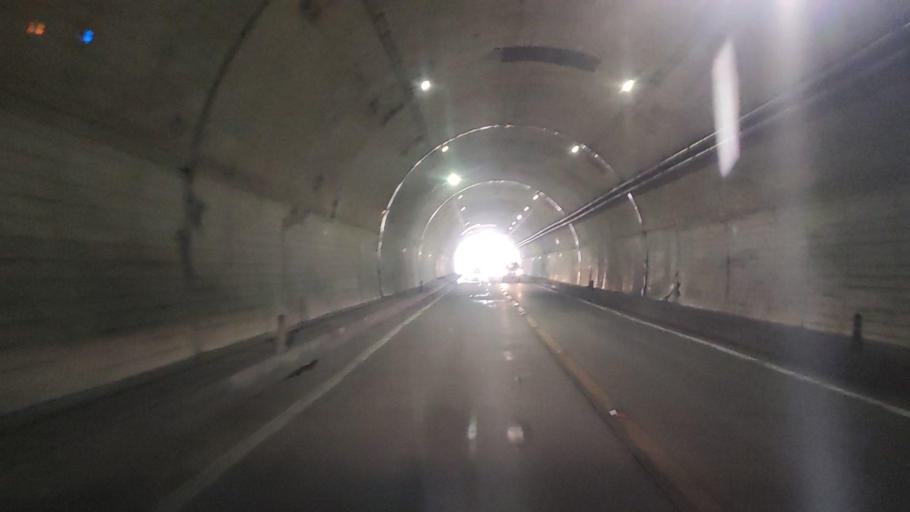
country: JP
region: Miyazaki
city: Nobeoka
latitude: 32.6316
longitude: 131.7312
